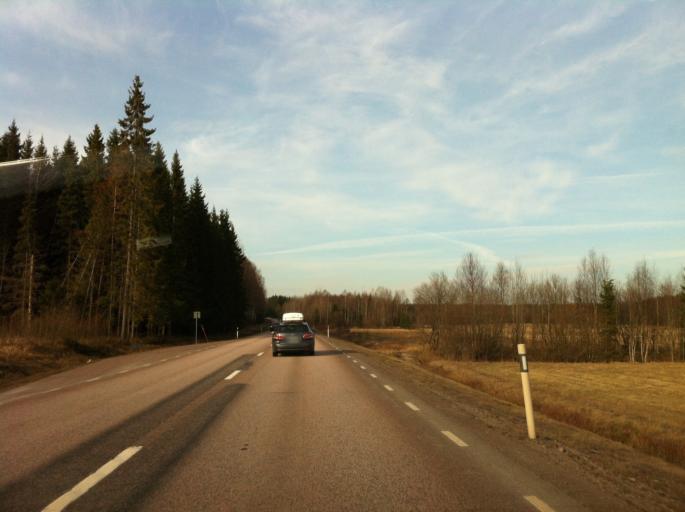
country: SE
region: Vaermland
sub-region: Kristinehamns Kommun
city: Bjorneborg
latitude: 59.2163
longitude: 14.1840
